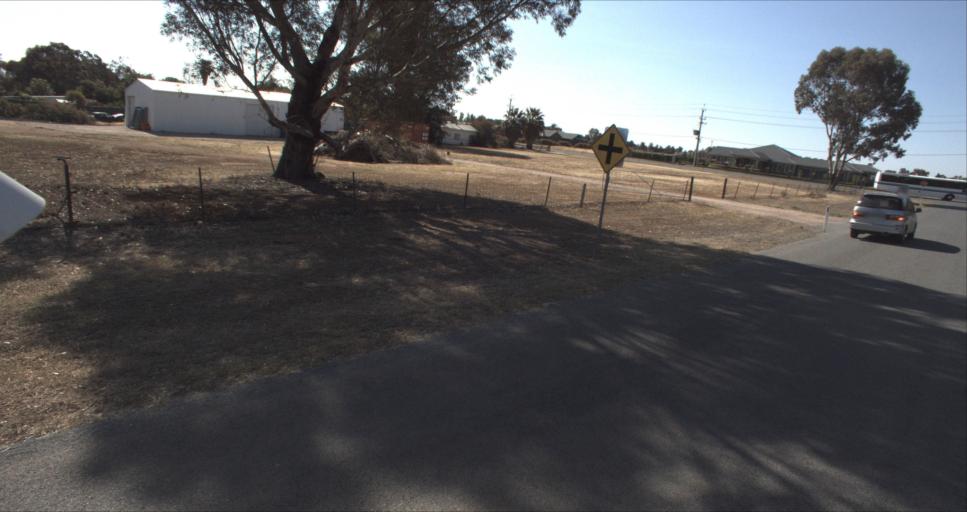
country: AU
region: New South Wales
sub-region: Leeton
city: Leeton
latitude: -34.5448
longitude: 146.4183
